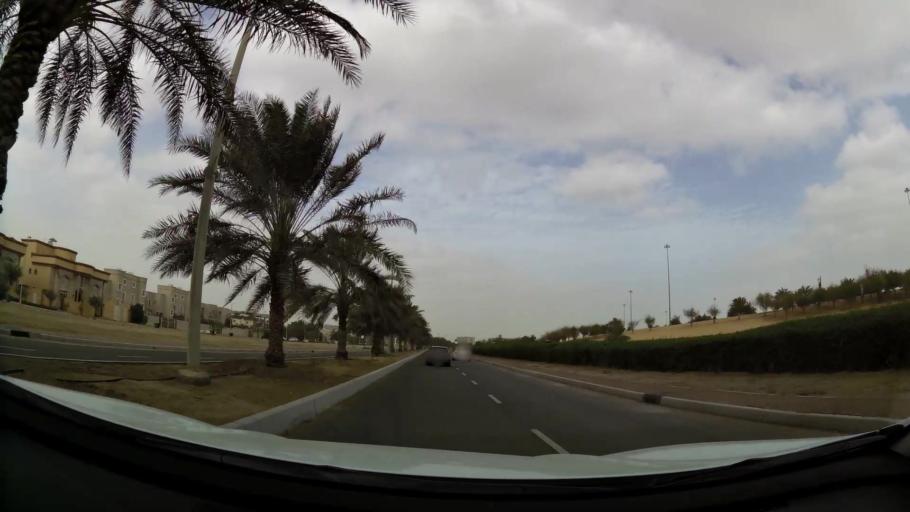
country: AE
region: Abu Dhabi
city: Abu Dhabi
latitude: 24.4126
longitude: 54.5036
